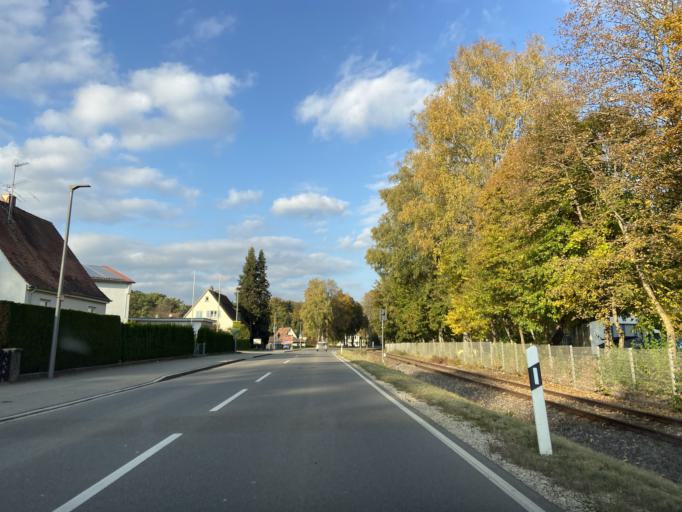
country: DE
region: Baden-Wuerttemberg
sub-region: Tuebingen Region
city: Sigmaringendorf
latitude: 48.0725
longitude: 9.2667
